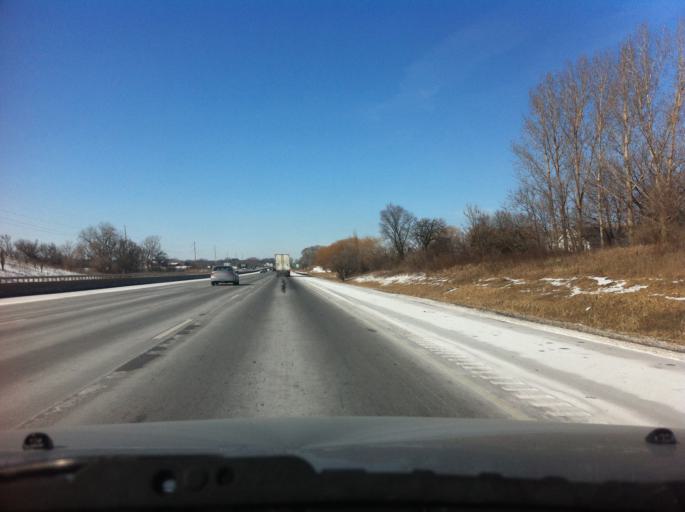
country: US
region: Wisconsin
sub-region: Dane County
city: Windsor
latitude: 43.2003
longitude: -89.3502
